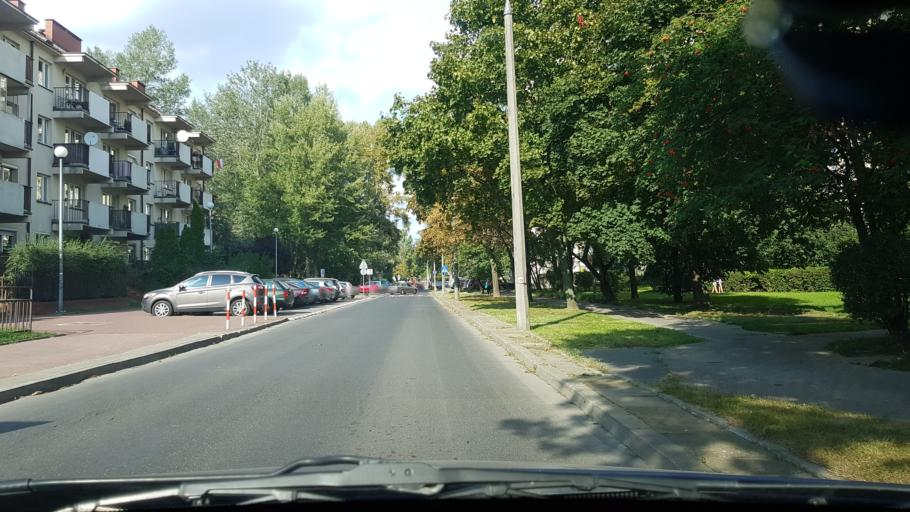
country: PL
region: Masovian Voivodeship
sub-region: Warszawa
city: Bielany
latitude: 52.2810
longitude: 20.9354
